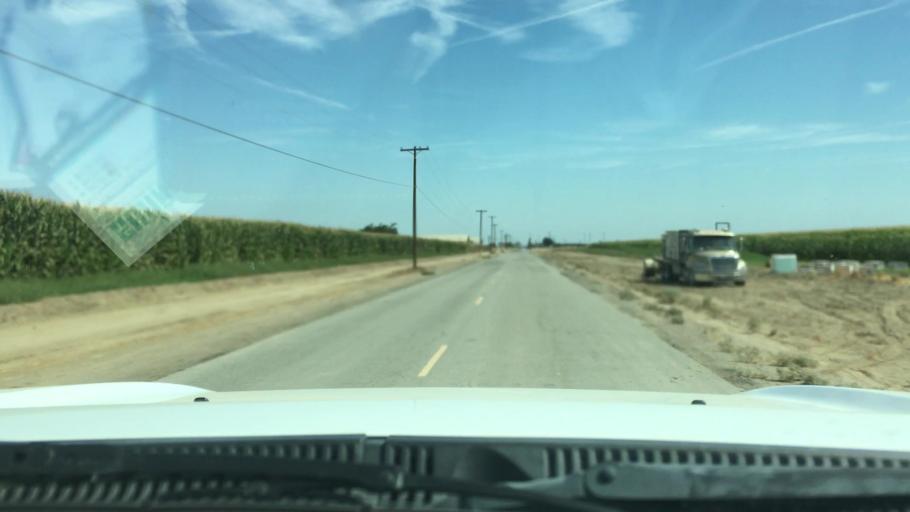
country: US
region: California
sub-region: Kern County
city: Buttonwillow
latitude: 35.4078
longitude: -119.3766
